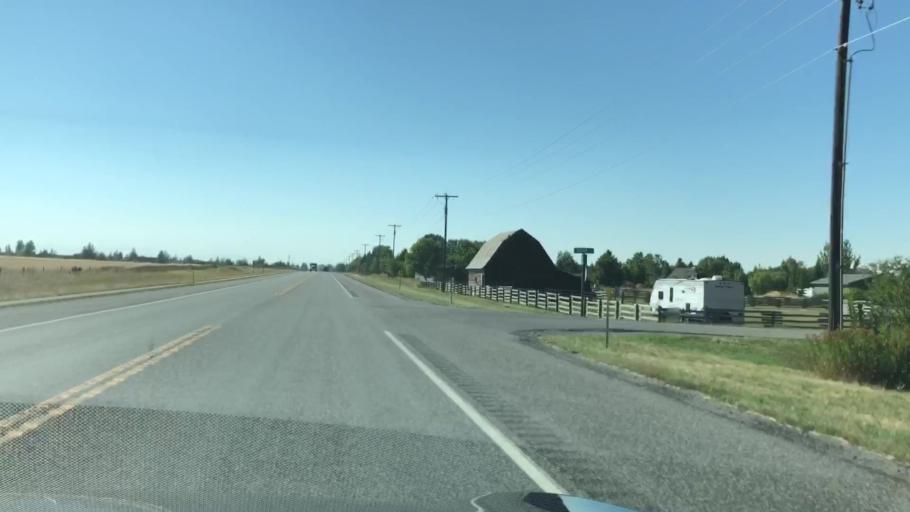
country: US
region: Montana
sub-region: Gallatin County
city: Belgrade
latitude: 45.7292
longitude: -111.1148
